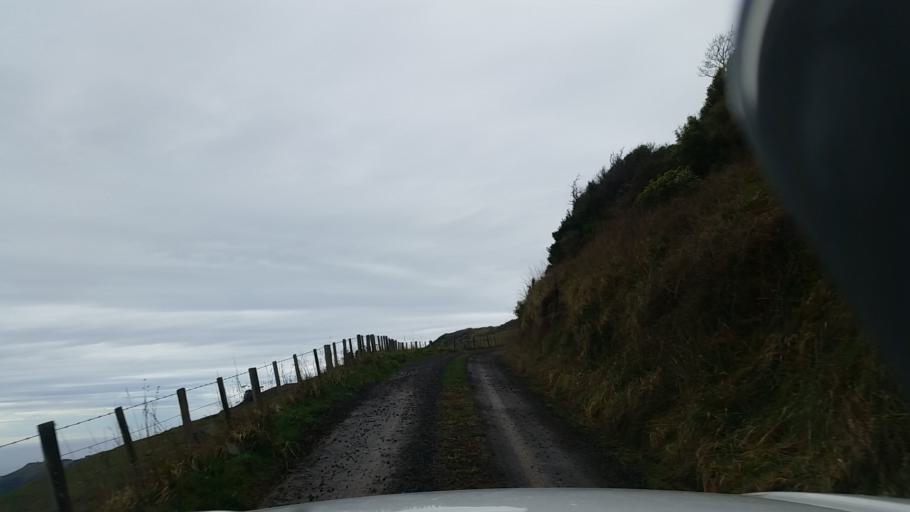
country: NZ
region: Canterbury
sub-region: Christchurch City
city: Christchurch
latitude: -43.7442
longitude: 173.0007
